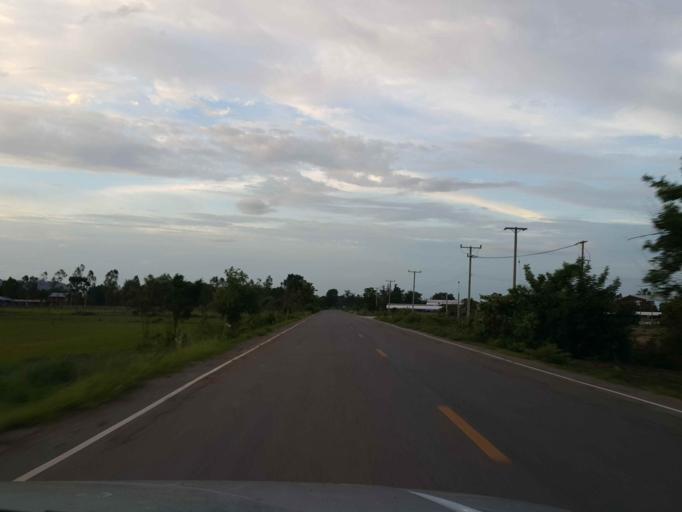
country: TH
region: Sukhothai
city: Ban Dan Lan Hoi
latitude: 17.0966
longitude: 99.5897
